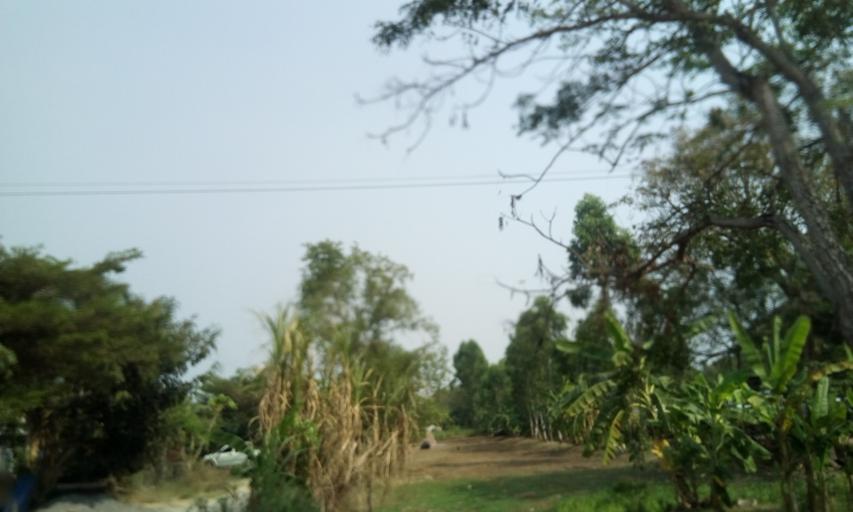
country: TH
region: Pathum Thani
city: Lam Luk Ka
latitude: 13.9539
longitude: 100.7250
